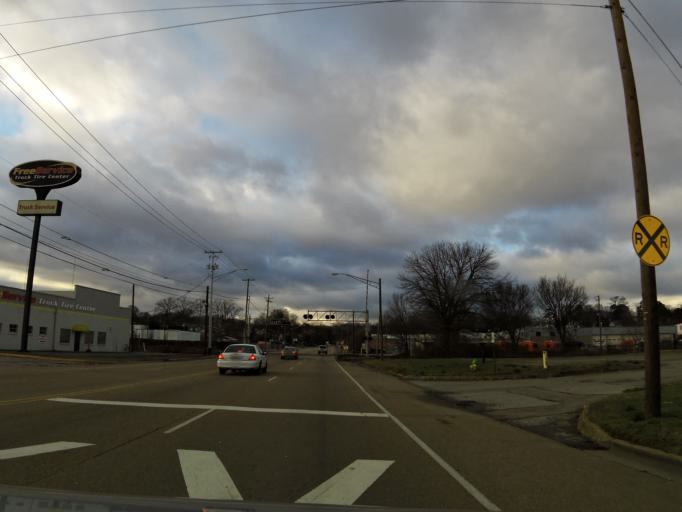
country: US
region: Tennessee
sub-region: Knox County
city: Knoxville
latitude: 35.9939
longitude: -83.9029
